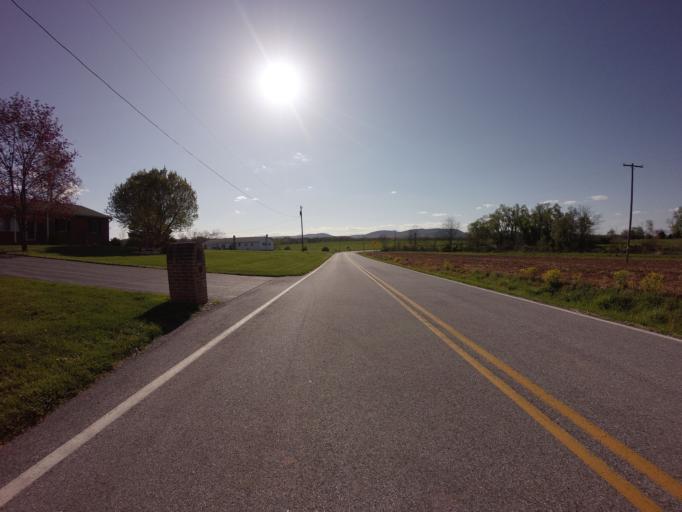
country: US
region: Maryland
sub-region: Frederick County
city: Emmitsburg
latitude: 39.6666
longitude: -77.2920
